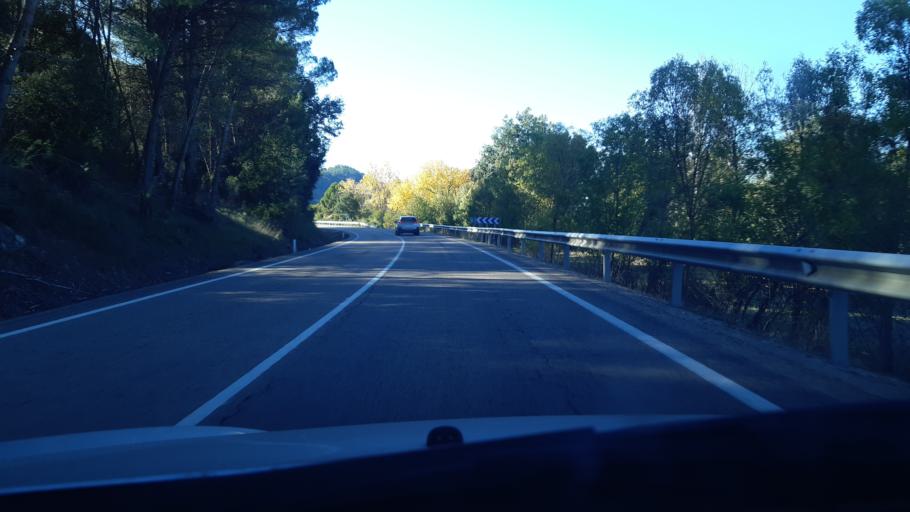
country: ES
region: Aragon
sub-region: Provincia de Teruel
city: Valderrobres
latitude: 40.8824
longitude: 0.1301
